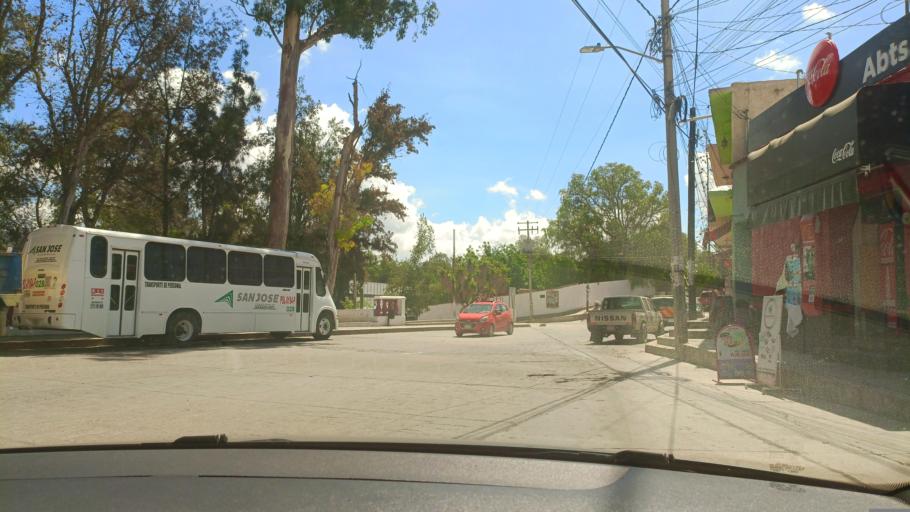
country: MX
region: Guanajuato
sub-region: San Luis de la Paz
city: San Luis de la Paz
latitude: 21.2983
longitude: -100.5089
